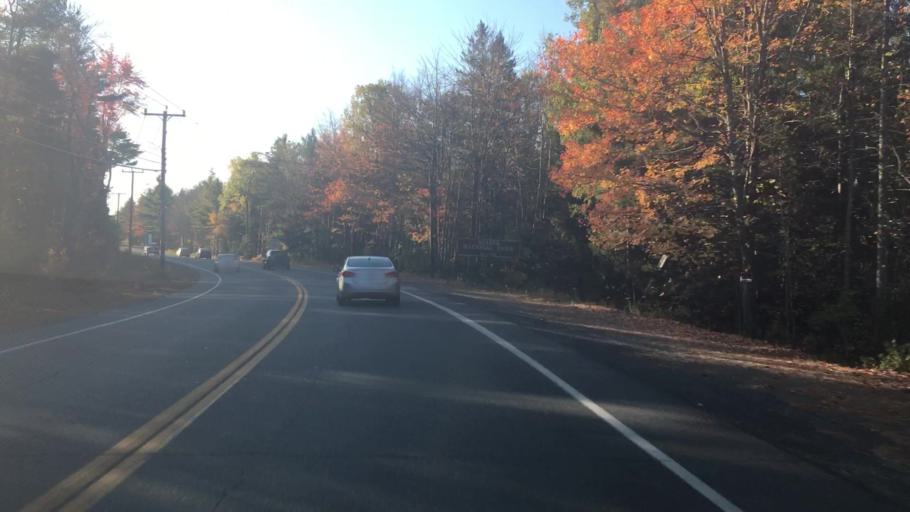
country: US
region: Maine
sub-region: Hancock County
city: Ellsworth
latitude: 44.5137
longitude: -68.3945
